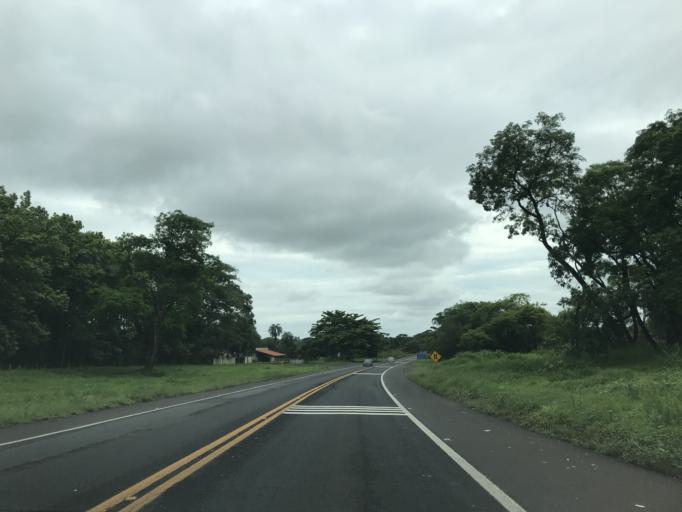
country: BR
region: Sao Paulo
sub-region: Nova Granada
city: Nova Granada
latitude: -20.4202
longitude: -49.2692
